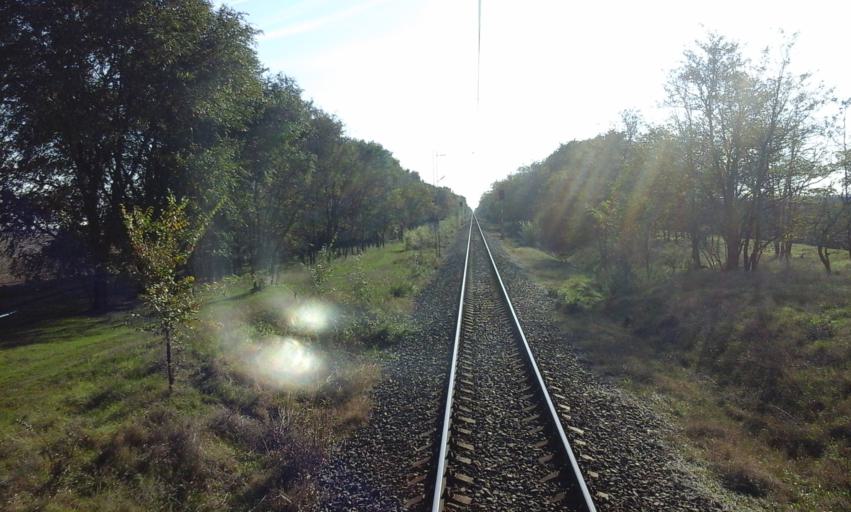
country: RS
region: Autonomna Pokrajina Vojvodina
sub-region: Severnobacki Okrug
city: Backa Topola
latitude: 45.8700
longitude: 19.6576
